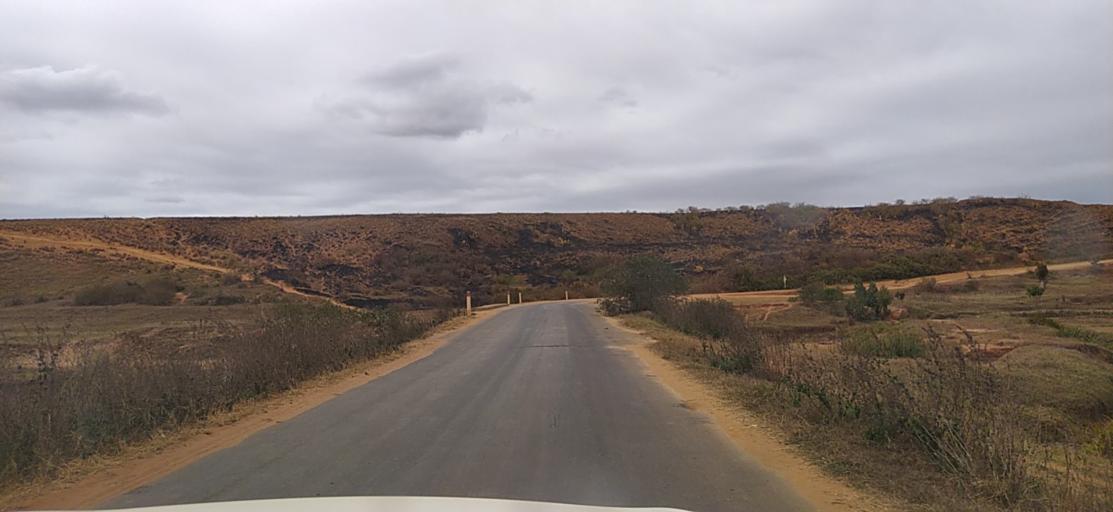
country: MG
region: Alaotra Mangoro
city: Ambatondrazaka
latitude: -17.9127
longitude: 48.2611
